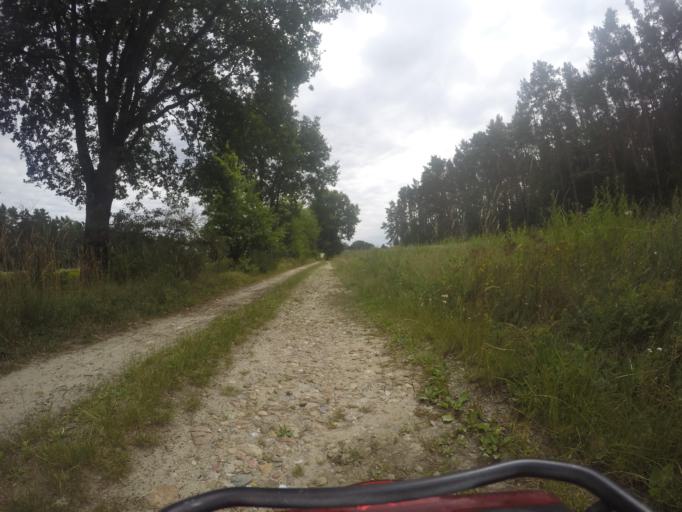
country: DE
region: Lower Saxony
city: Dahlem
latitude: 53.2177
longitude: 10.7397
